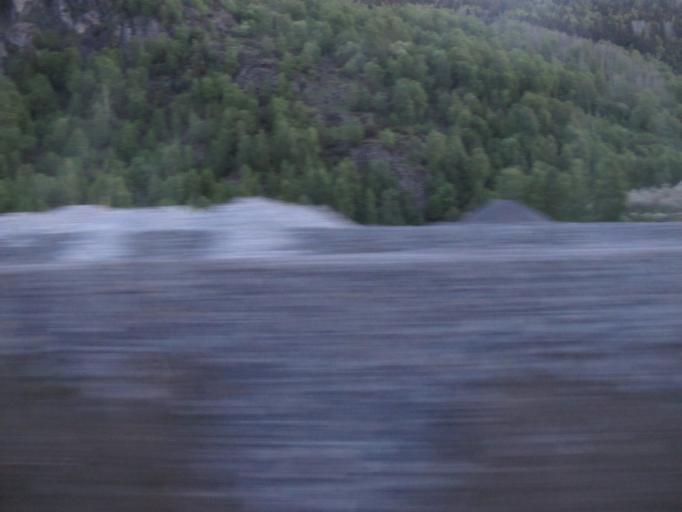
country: NO
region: Oppland
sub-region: Sor-Fron
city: Hundorp
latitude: 61.5481
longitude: 10.0120
